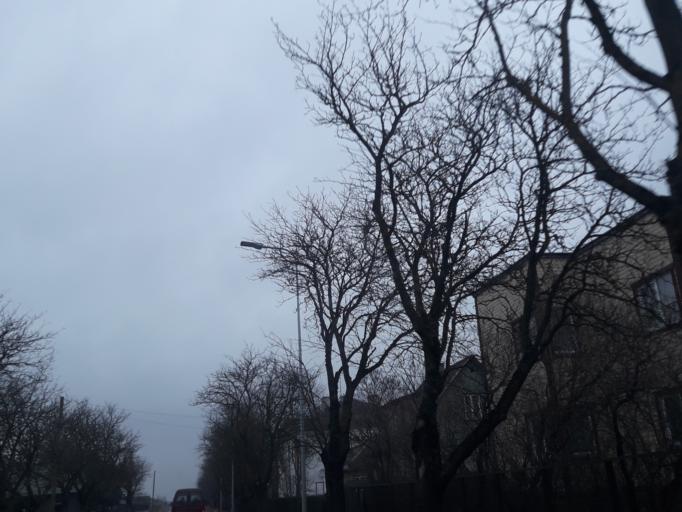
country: EE
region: Saare
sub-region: Kuressaare linn
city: Kuressaare
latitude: 58.2539
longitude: 22.4770
